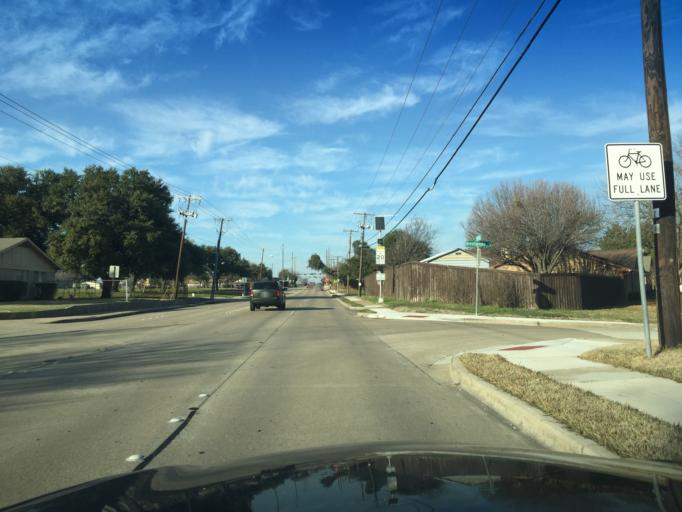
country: US
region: Texas
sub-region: Dallas County
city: Carrollton
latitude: 32.9824
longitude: -96.8835
